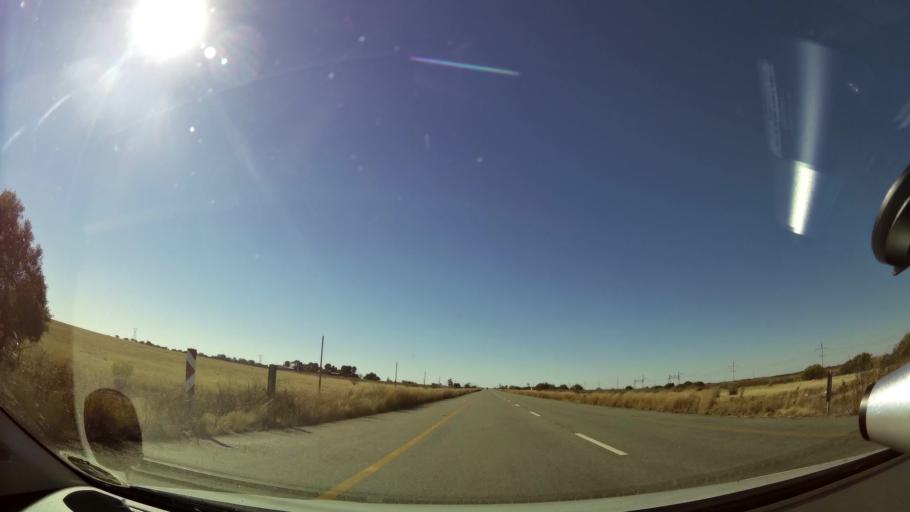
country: ZA
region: North-West
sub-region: Dr Ruth Segomotsi Mompati District Municipality
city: Bloemhof
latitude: -27.6808
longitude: 25.4596
